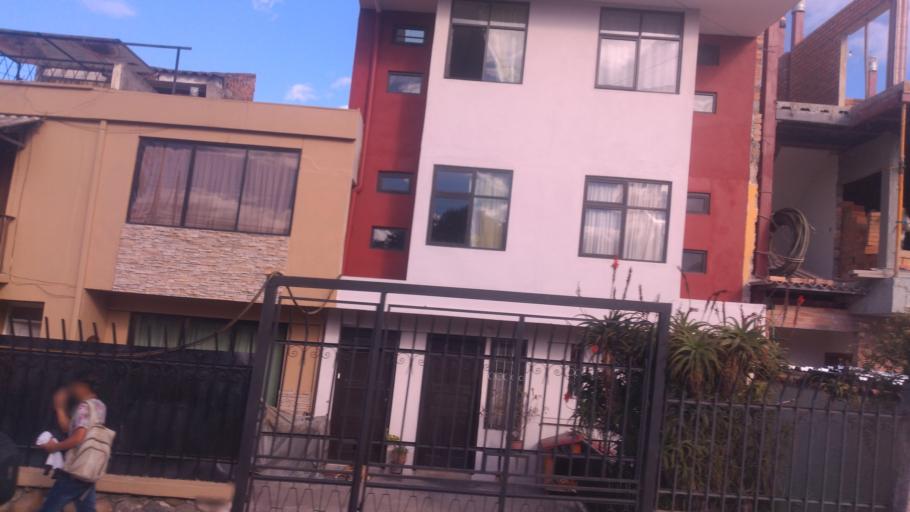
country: EC
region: Azuay
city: Cuenca
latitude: -2.8990
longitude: -79.0137
